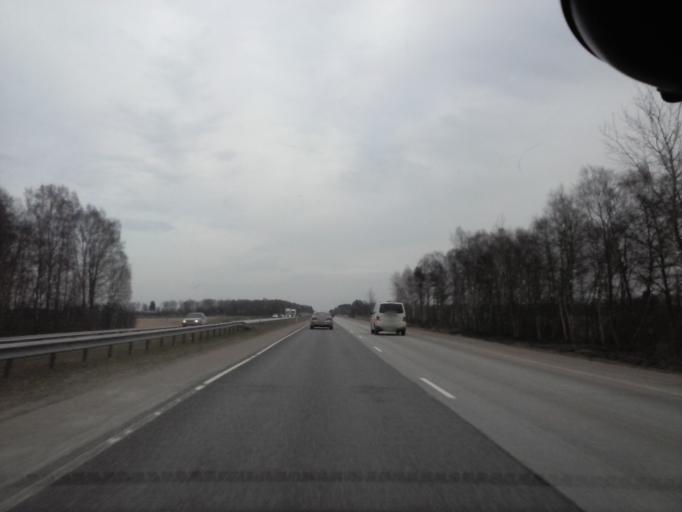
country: EE
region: Harju
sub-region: Rae vald
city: Jueri
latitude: 59.3331
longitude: 24.9109
